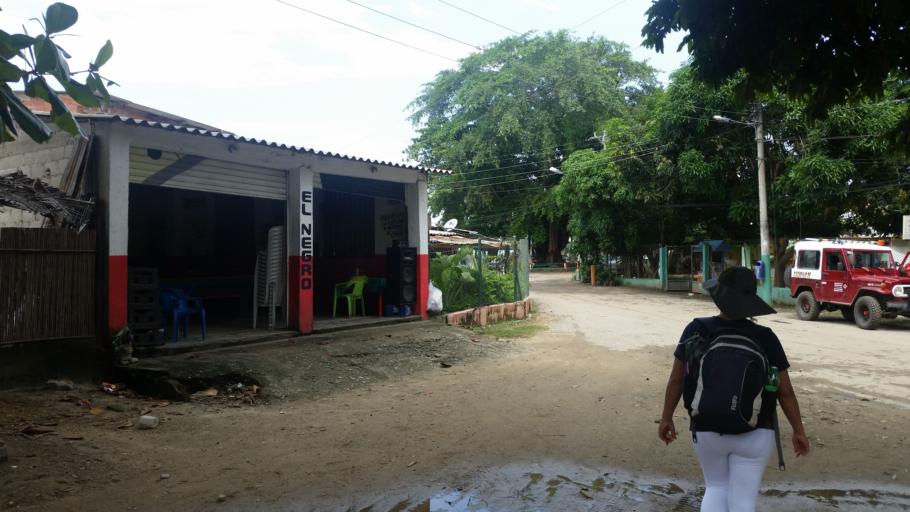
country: CO
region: Magdalena
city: Santa Marta
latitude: 11.2611
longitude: -73.7685
